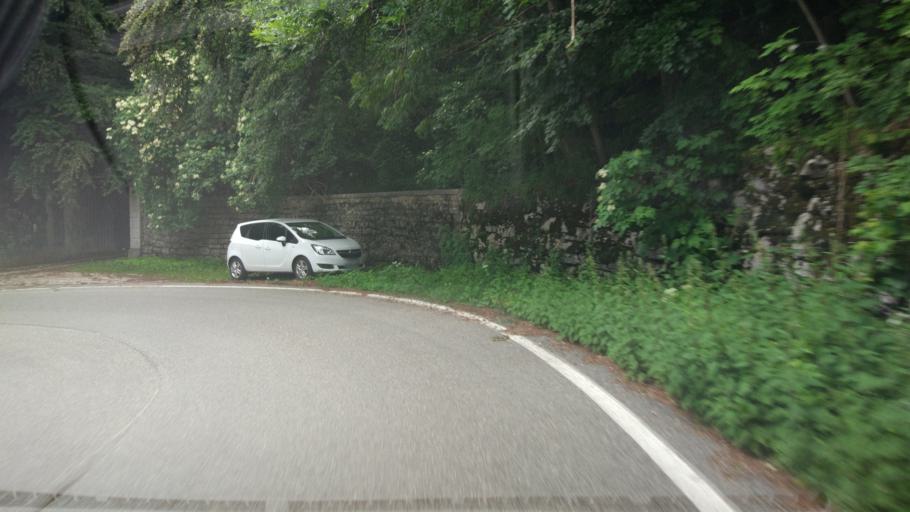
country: IT
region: Veneto
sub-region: Provincia di Verona
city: Bosco Chiesanuova
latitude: 45.6282
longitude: 11.0354
